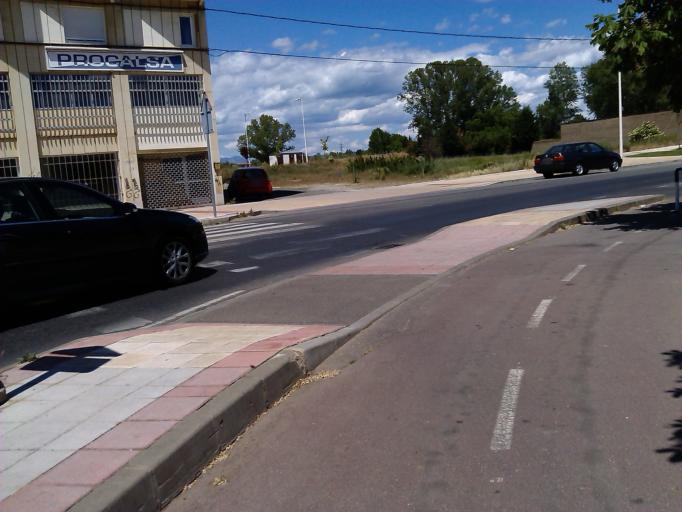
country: ES
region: Castille and Leon
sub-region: Provincia de Leon
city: Leon
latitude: 42.6004
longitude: -5.5564
